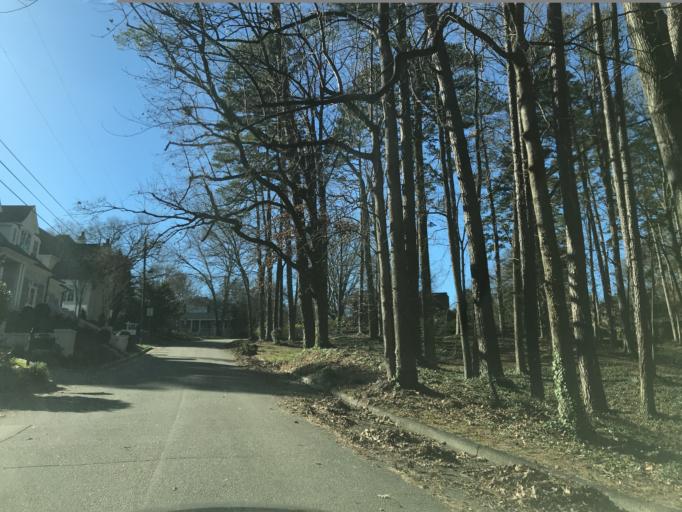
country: US
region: North Carolina
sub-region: Wake County
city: West Raleigh
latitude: 35.8147
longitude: -78.6467
